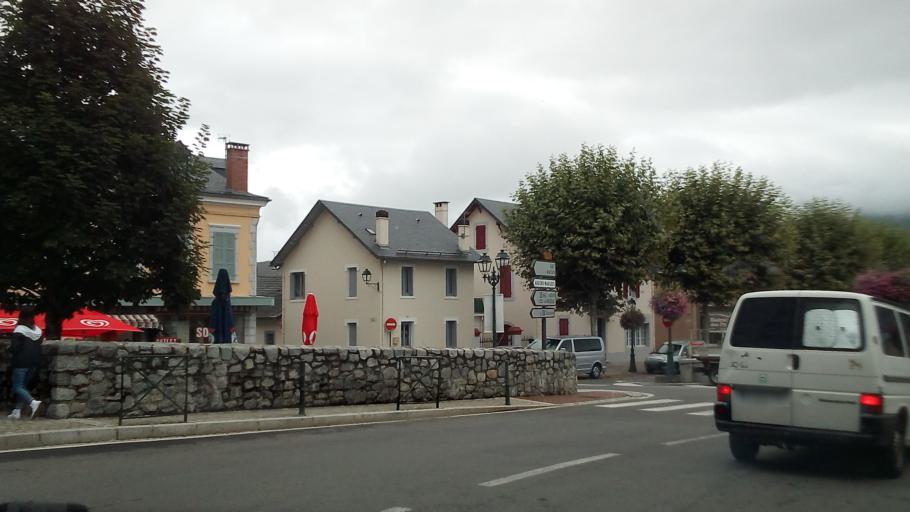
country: FR
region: Midi-Pyrenees
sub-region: Departement des Hautes-Pyrenees
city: Argeles-Gazost
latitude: 43.0070
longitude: -0.1015
